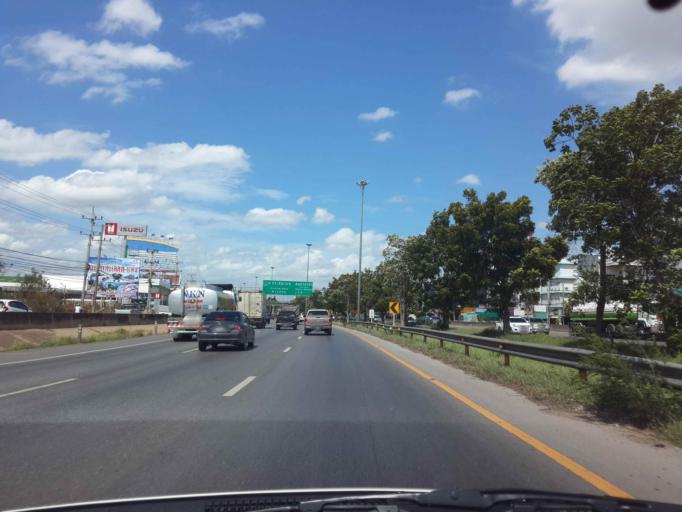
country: TH
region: Samut Sakhon
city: Samut Sakhon
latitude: 13.5457
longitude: 100.2579
